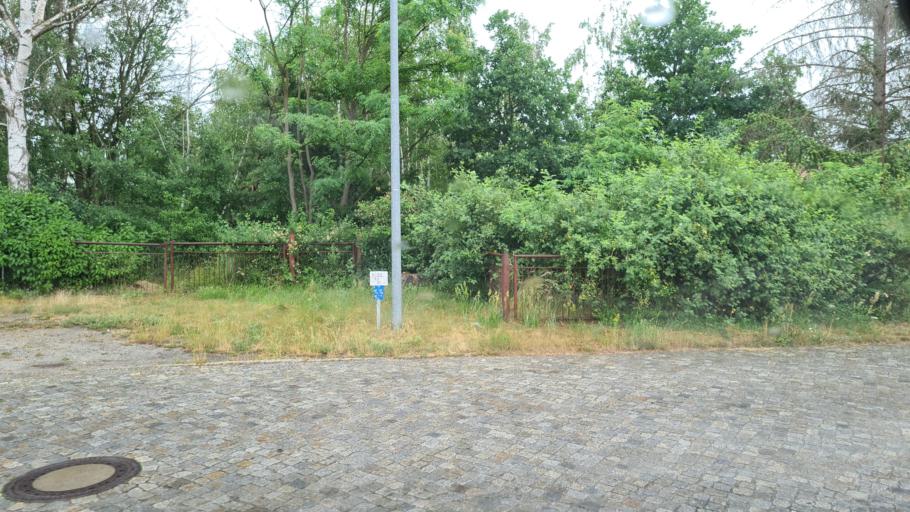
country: DE
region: Brandenburg
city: Lauchhammer
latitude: 51.4836
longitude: 13.7265
